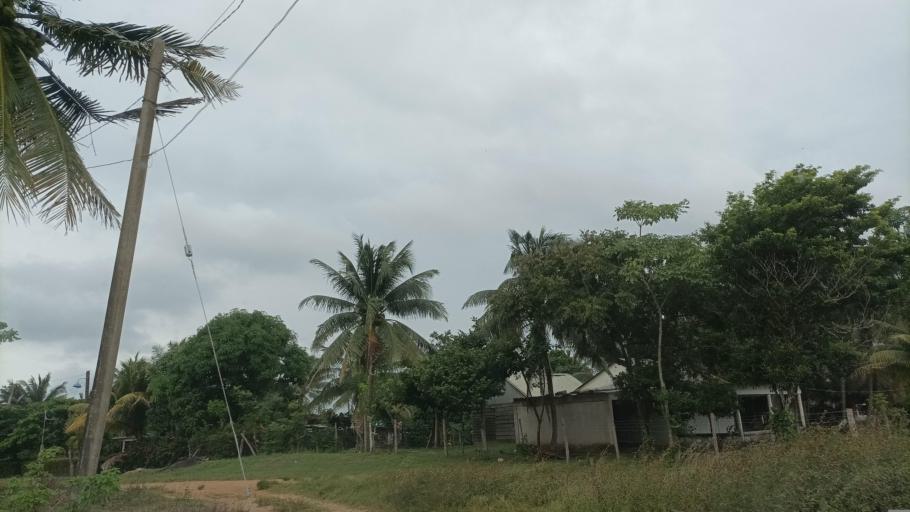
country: MX
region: Veracruz
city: Agua Dulce
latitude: 18.2066
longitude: -94.1440
